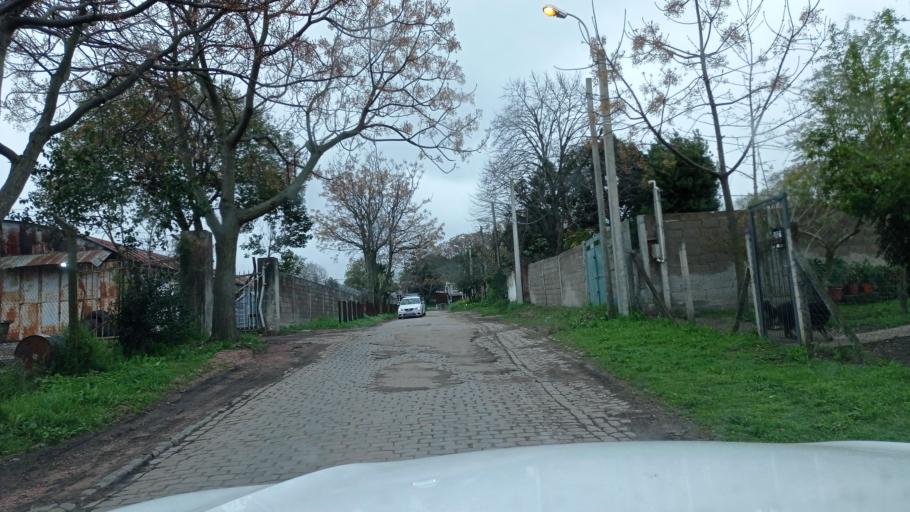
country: UY
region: Montevideo
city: Montevideo
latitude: -34.8507
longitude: -56.2156
